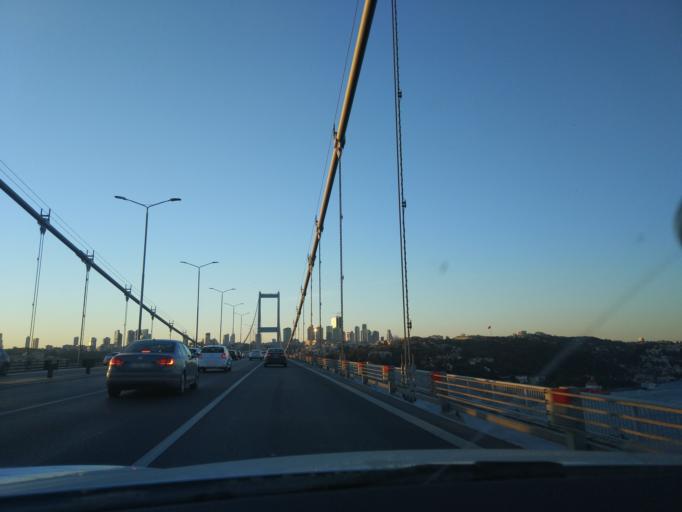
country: TR
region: Istanbul
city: UEskuedar
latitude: 41.0439
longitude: 29.0361
